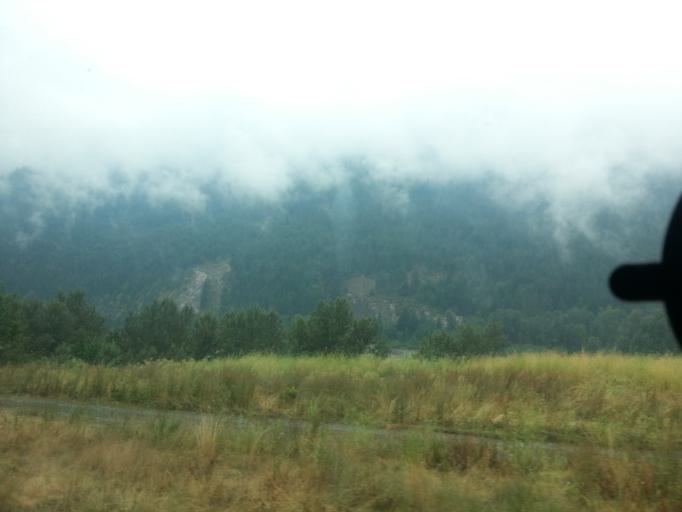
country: CA
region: British Columbia
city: Hope
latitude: 49.8456
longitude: -121.4344
